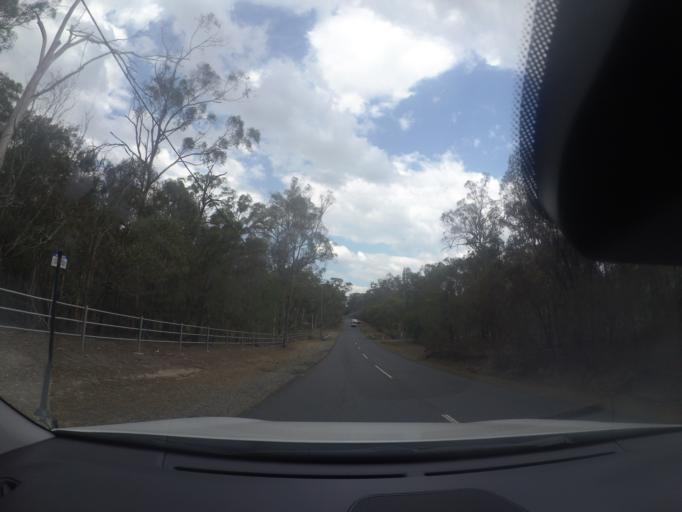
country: AU
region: Queensland
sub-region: Logan
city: Woodridge
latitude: -27.6244
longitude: 153.0951
